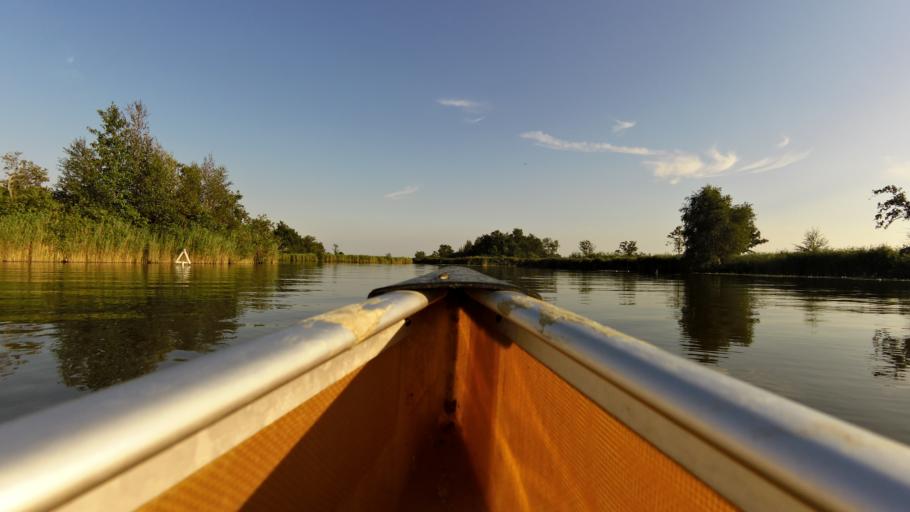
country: NL
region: South Holland
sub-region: Gemeente Nieuwkoop
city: Nieuwkoop
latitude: 52.1363
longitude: 4.7753
